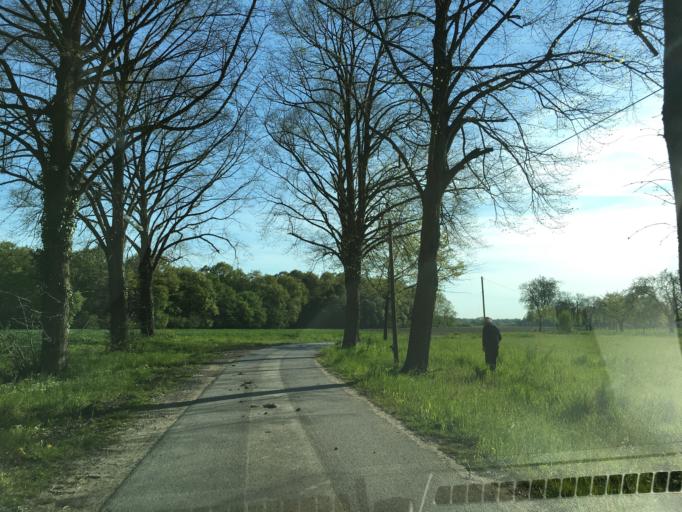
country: DE
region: North Rhine-Westphalia
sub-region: Regierungsbezirk Munster
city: Nordkirchen
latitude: 51.7553
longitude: 7.5054
